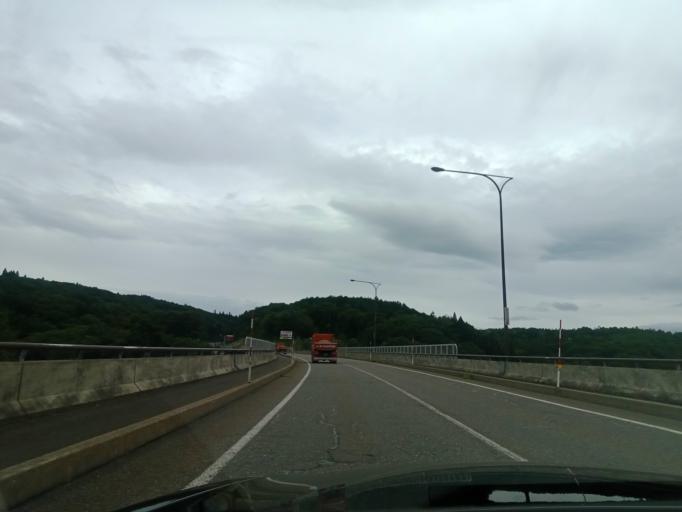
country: JP
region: Niigata
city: Arai
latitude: 36.8516
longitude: 138.1933
